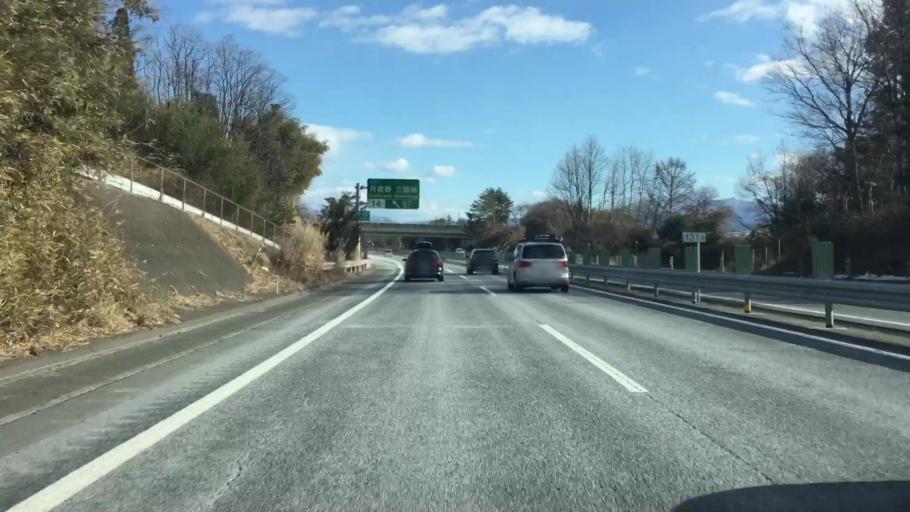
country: JP
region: Gunma
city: Numata
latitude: 36.6776
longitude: 139.0141
